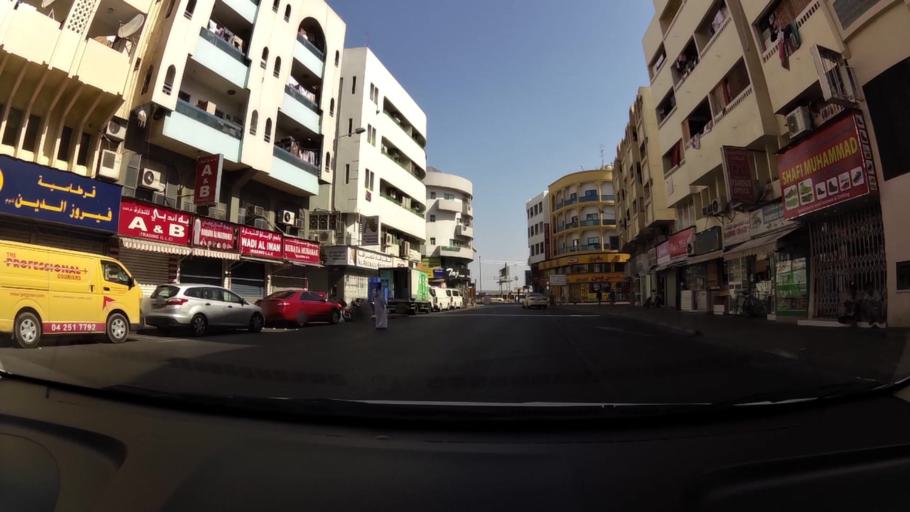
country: AE
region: Ash Shariqah
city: Sharjah
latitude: 25.2742
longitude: 55.3021
